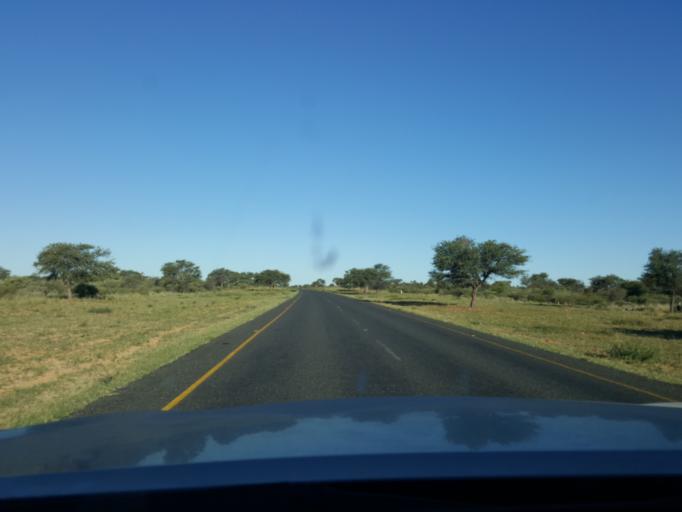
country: BW
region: Southern
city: Khakhea
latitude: -24.2239
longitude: 23.2363
